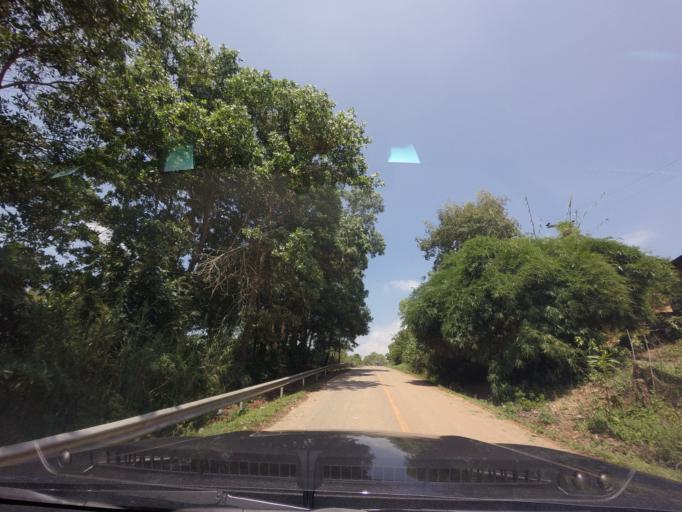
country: TH
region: Loei
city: Na Haeo
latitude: 17.5952
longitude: 100.9041
